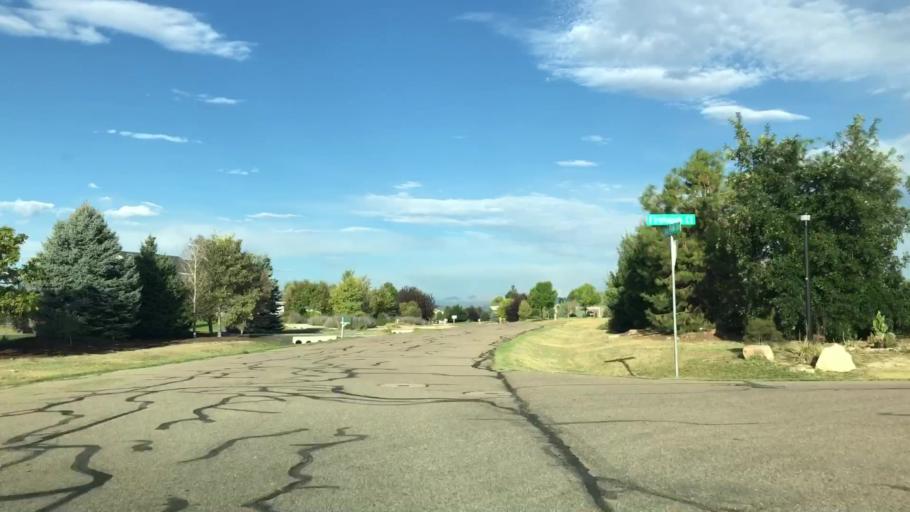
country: US
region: Colorado
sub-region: Weld County
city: Windsor
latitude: 40.4375
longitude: -104.9547
